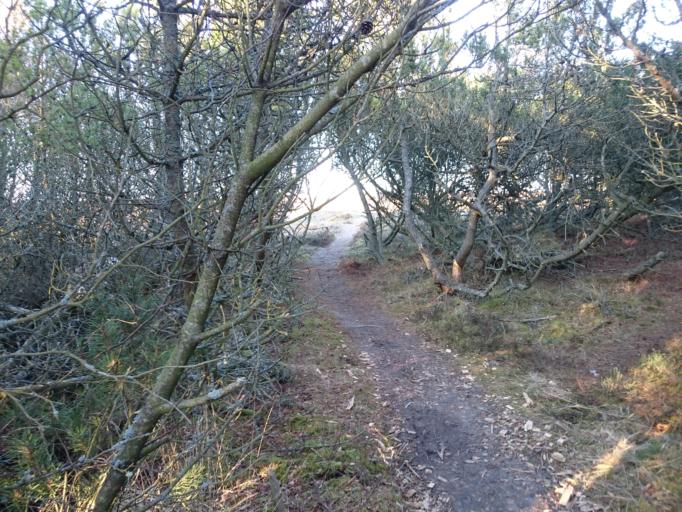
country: DK
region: North Denmark
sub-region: Frederikshavn Kommune
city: Skagen
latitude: 57.7411
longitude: 10.6107
